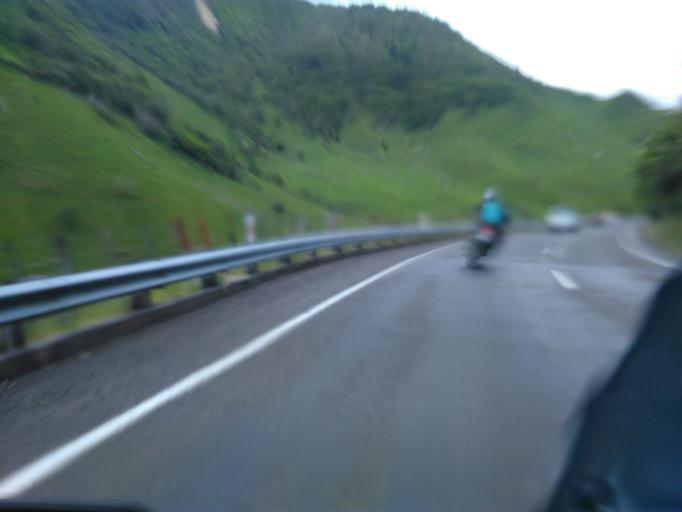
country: NZ
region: Bay of Plenty
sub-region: Opotiki District
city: Opotiki
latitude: -38.3595
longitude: 177.4600
